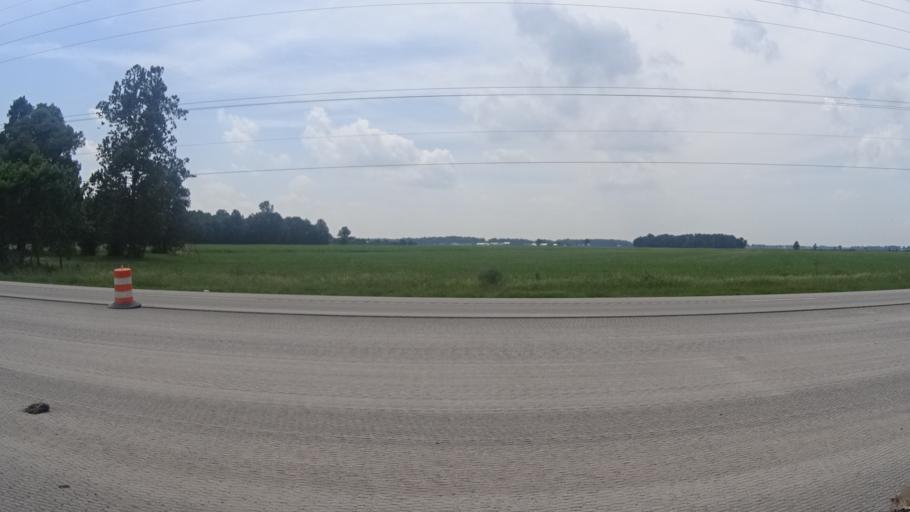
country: US
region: Ohio
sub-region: Erie County
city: Milan
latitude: 41.3139
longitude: -82.6088
